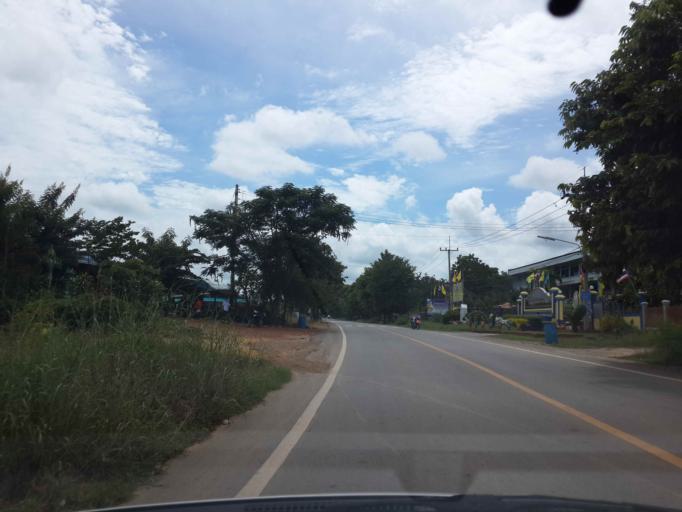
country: TH
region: Ratchaburi
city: Pak Tho
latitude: 13.4146
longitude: 99.6729
